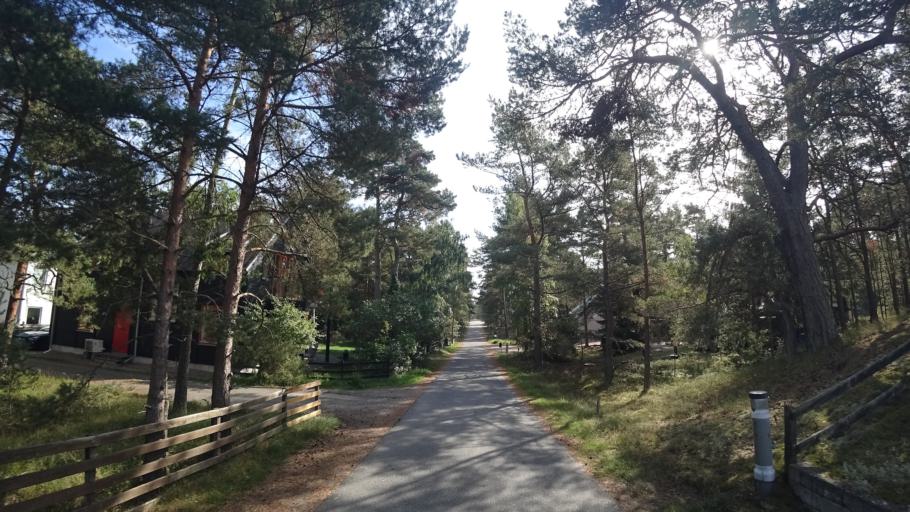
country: SE
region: Skane
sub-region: Kristianstads Kommun
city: Ahus
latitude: 55.9172
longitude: 14.2962
